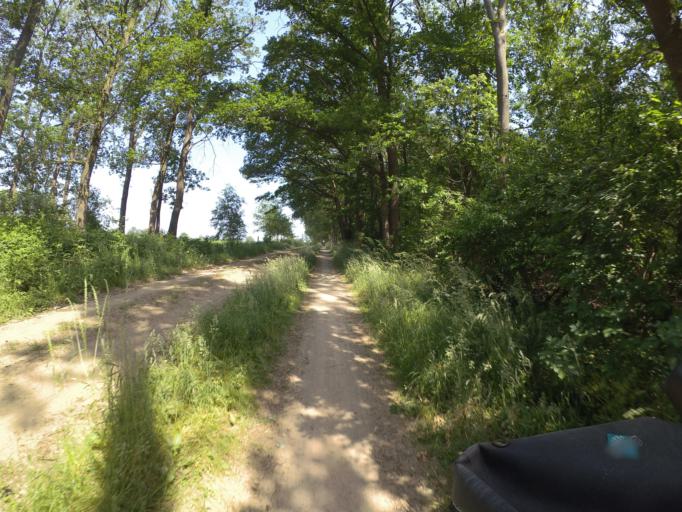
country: NL
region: Overijssel
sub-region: Gemeente Hof van Twente
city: Markelo
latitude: 52.2293
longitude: 6.5234
